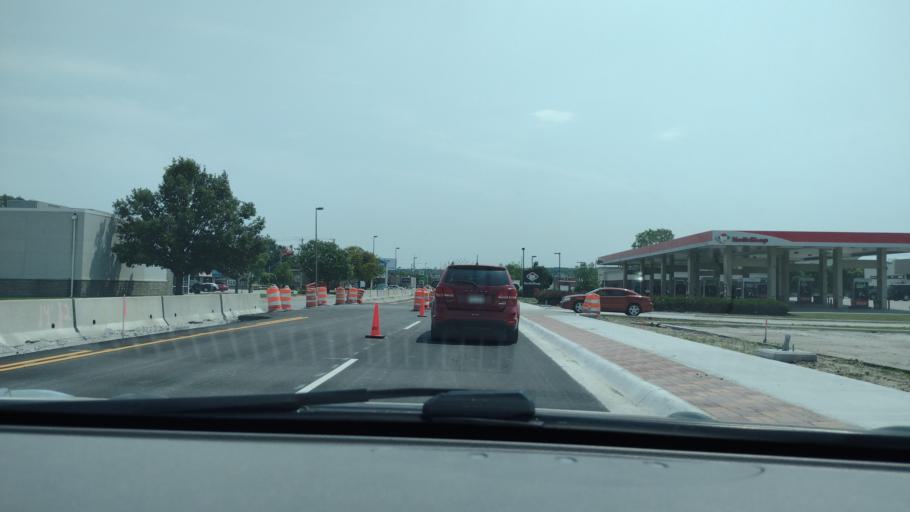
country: US
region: Iowa
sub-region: Pottawattamie County
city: Council Bluffs
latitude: 41.2618
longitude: -95.8712
